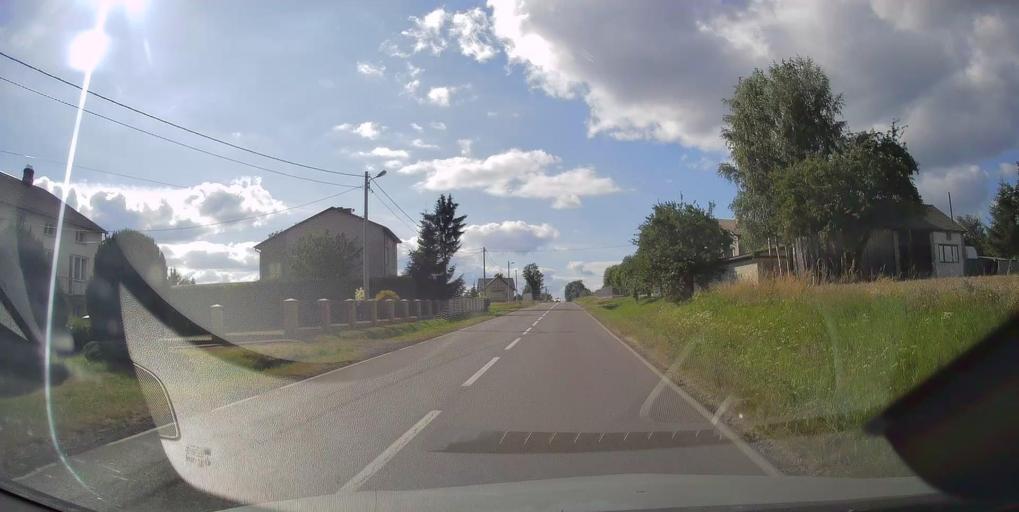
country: PL
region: Swietokrzyskie
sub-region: Powiat kielecki
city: Bodzentyn
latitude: 50.9697
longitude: 20.8838
